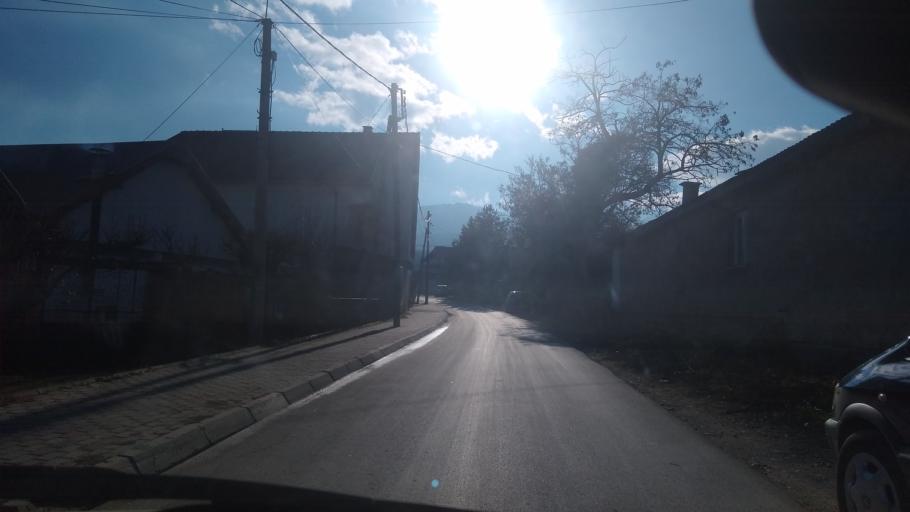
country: MK
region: Bitola
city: Bitola
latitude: 41.0101
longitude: 21.3459
